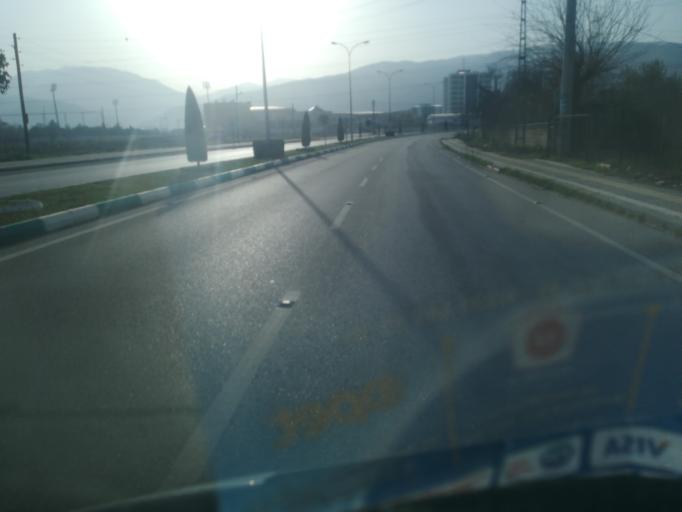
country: TR
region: Osmaniye
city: Osmaniye
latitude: 37.0565
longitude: 36.2207
